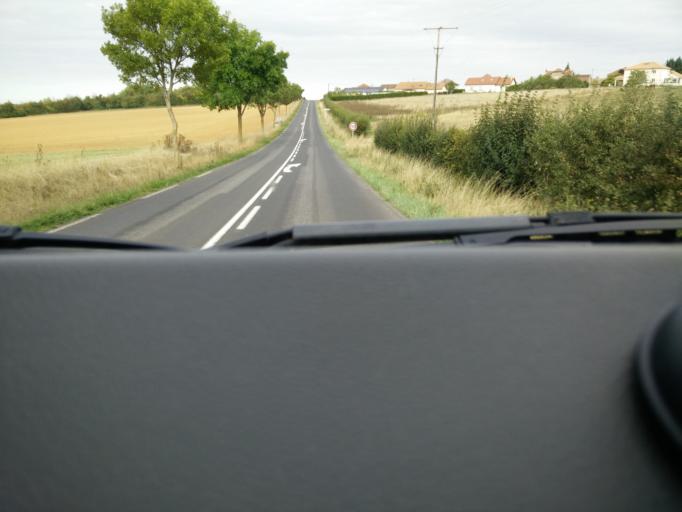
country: FR
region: Lorraine
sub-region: Departement de Meurthe-et-Moselle
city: Montauville
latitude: 48.9000
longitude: 5.9622
